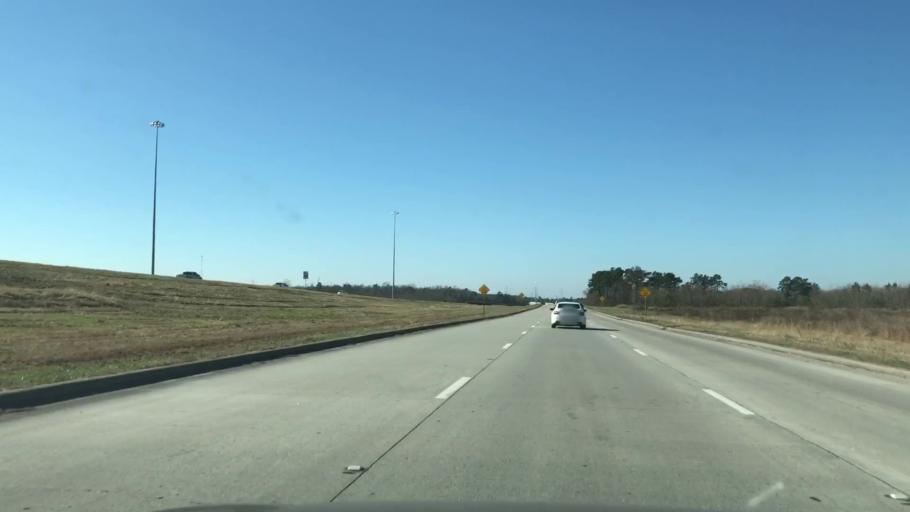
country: US
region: Texas
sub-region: Harris County
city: Cloverleaf
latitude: 29.8298
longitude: -95.1840
